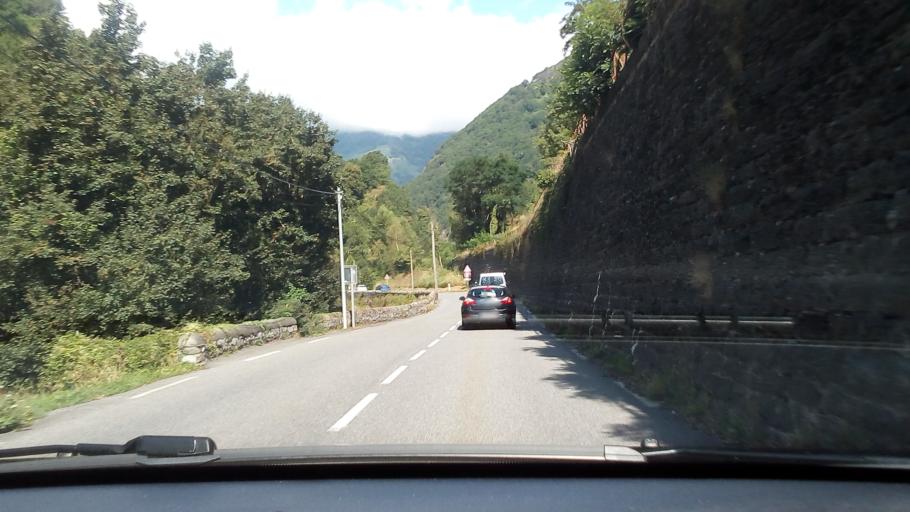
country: FR
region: Aquitaine
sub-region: Departement des Pyrenees-Atlantiques
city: Laruns
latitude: 42.9320
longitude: -0.5837
